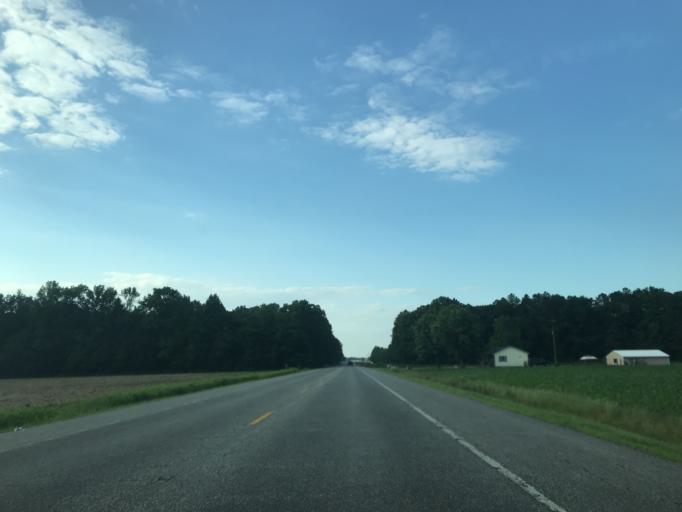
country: US
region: Maryland
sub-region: Caroline County
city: Federalsburg
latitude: 38.7878
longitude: -75.7871
